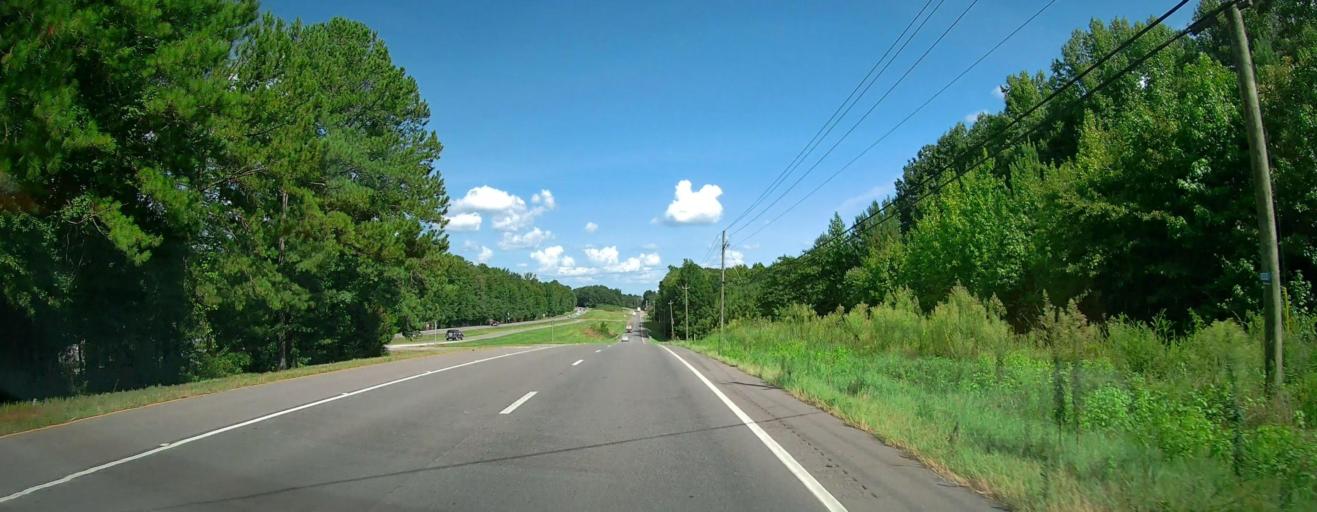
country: US
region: Alabama
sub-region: Tuscaloosa County
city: Northport
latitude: 33.2412
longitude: -87.6639
